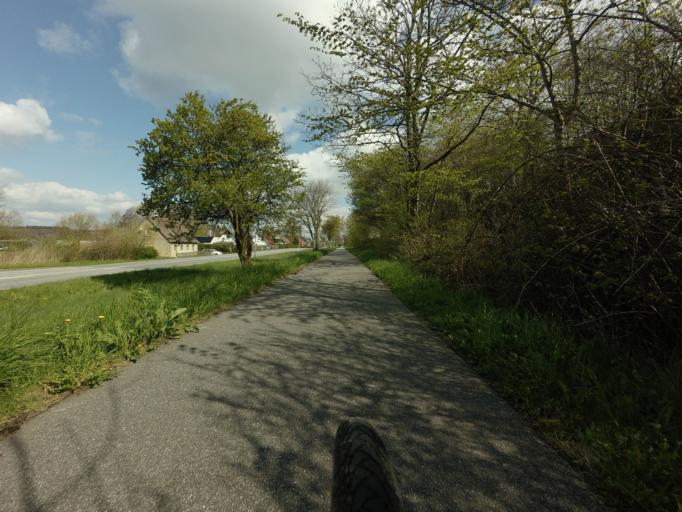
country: DK
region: North Denmark
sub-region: Mariagerfjord Kommune
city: Hadsund
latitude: 56.7003
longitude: 10.1141
